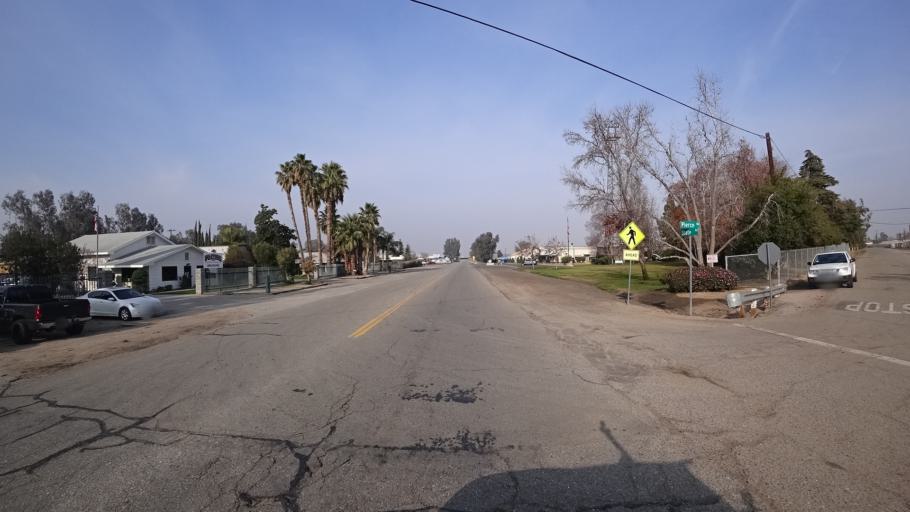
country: US
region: California
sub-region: Kern County
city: Oildale
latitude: 35.4046
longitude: -119.0433
